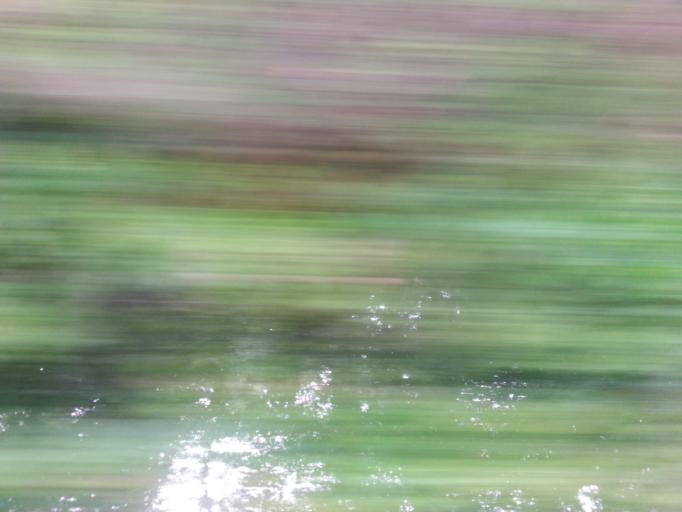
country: US
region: Tennessee
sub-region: Sevier County
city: Seymour
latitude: 35.8450
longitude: -83.7795
